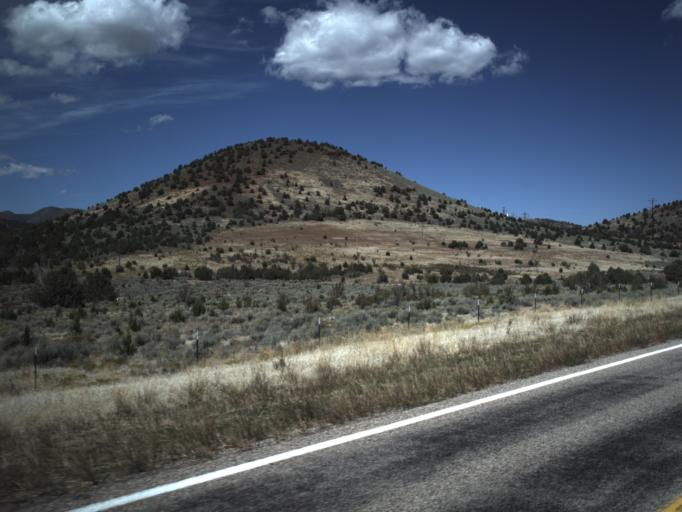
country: US
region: Utah
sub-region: Washington County
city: Enterprise
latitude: 37.3964
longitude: -113.6437
